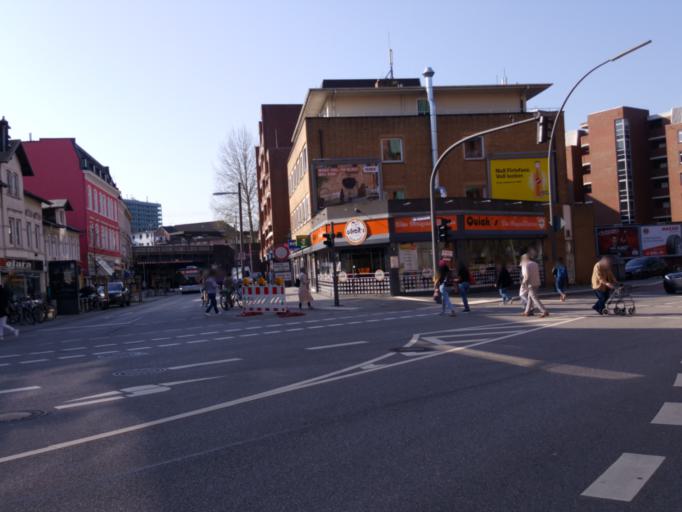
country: DE
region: Hamburg
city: Bergedorf
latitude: 53.4919
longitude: 10.2075
